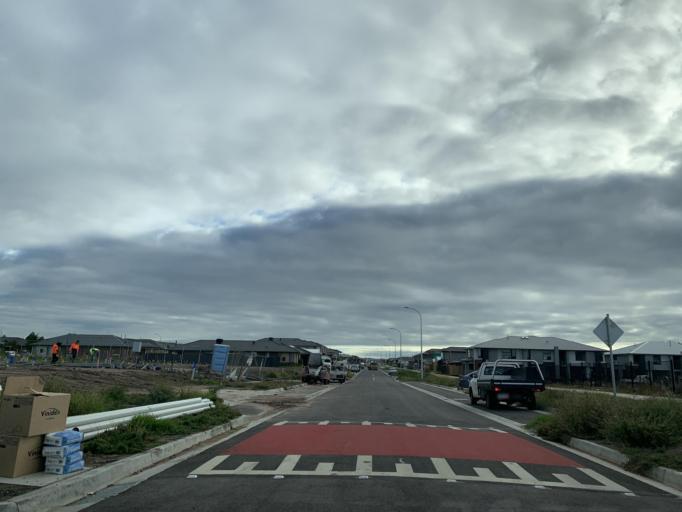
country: AU
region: Victoria
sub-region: Casey
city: Cranbourne East
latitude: -38.1279
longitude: 145.3353
